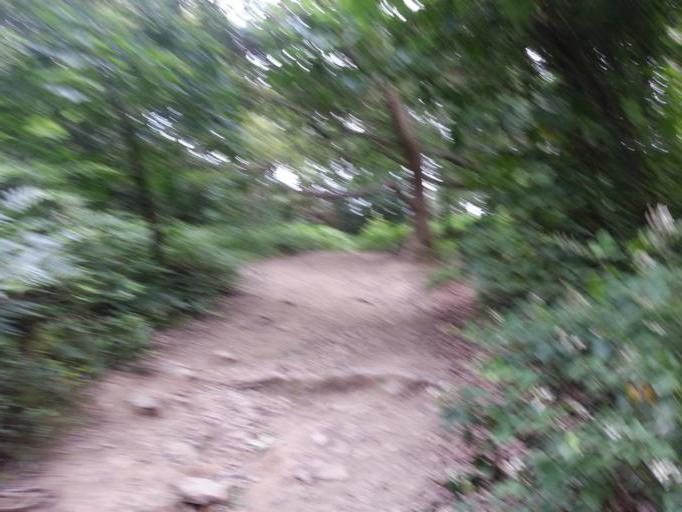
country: IE
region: Leinster
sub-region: Wicklow
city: Bray
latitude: 53.1924
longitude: -6.0881
